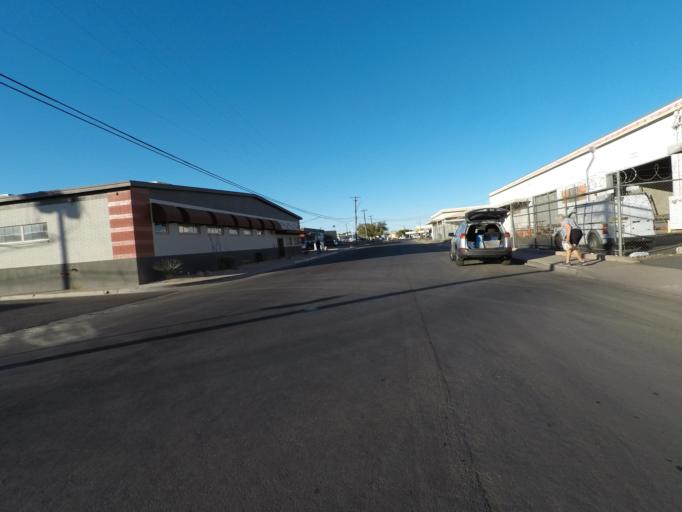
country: US
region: Arizona
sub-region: Maricopa County
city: Phoenix
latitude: 33.4695
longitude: -112.1063
